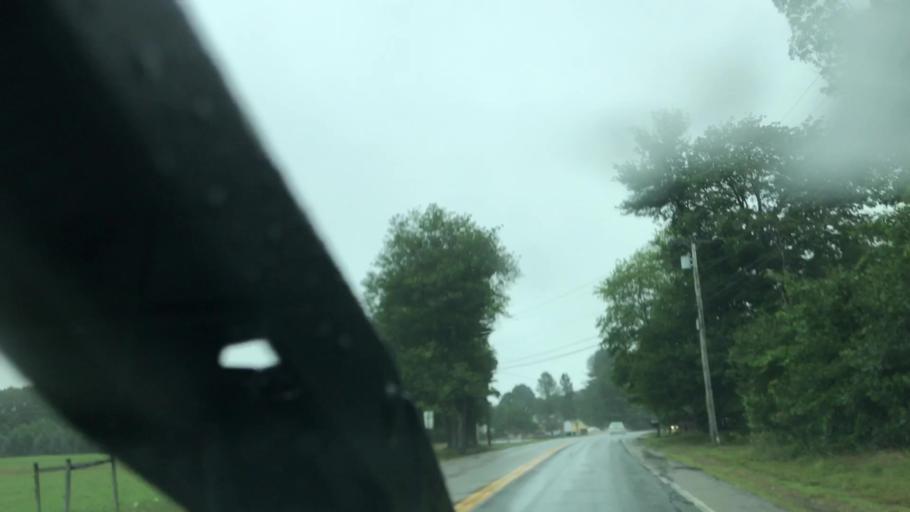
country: US
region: Maine
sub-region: York County
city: North Berwick
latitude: 43.2922
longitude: -70.7865
